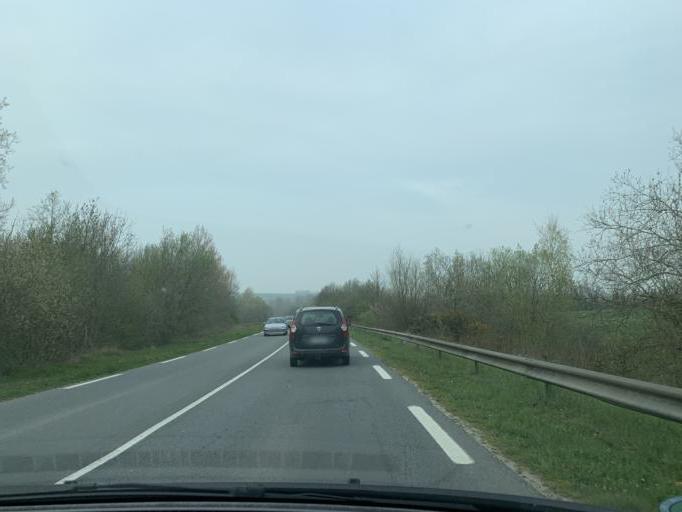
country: FR
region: Nord-Pas-de-Calais
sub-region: Departement du Pas-de-Calais
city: Montreuil
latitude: 50.4608
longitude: 1.7740
